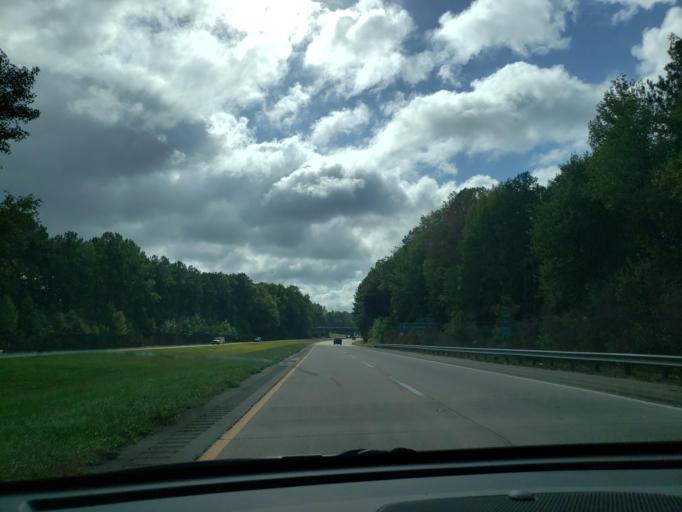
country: US
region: North Carolina
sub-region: Vance County
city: Henderson
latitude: 36.3368
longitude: -78.4338
